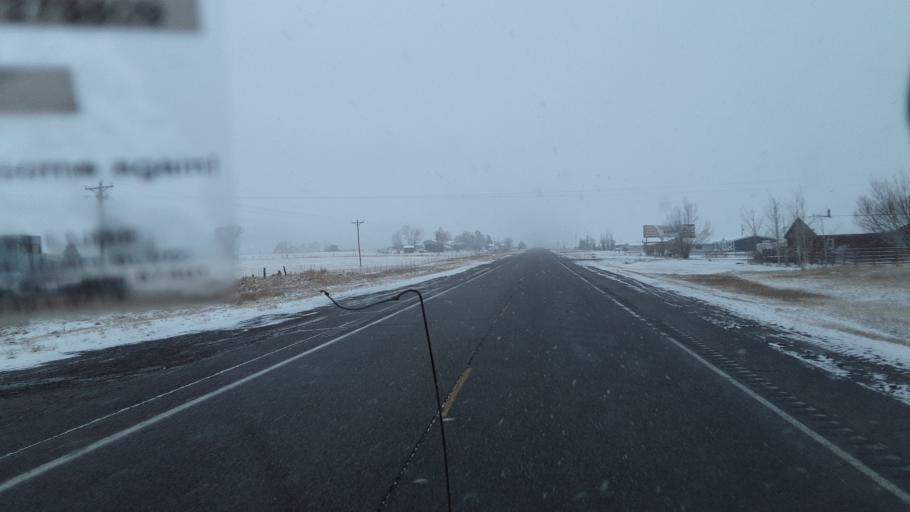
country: US
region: New Mexico
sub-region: Rio Arriba County
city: Chama
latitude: 36.8845
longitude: -106.6077
